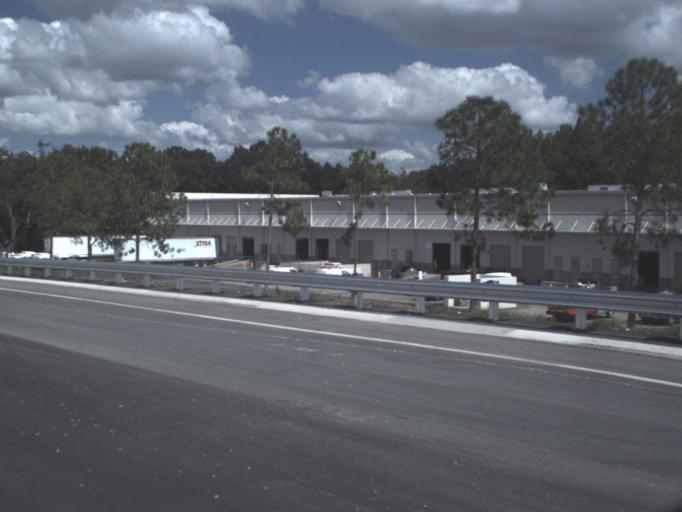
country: US
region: Florida
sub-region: Hillsborough County
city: Town 'n' Country
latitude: 28.0170
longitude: -82.5452
